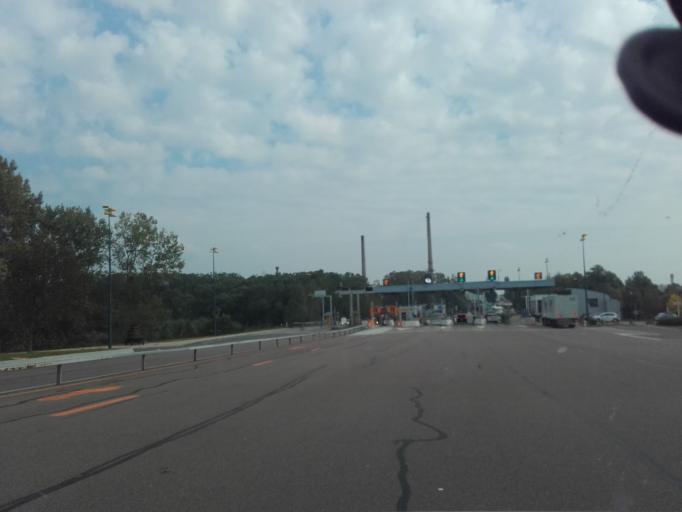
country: FR
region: Bourgogne
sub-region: Departement de Saone-et-Loire
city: Champforgeuil
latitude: 46.8032
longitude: 4.8285
